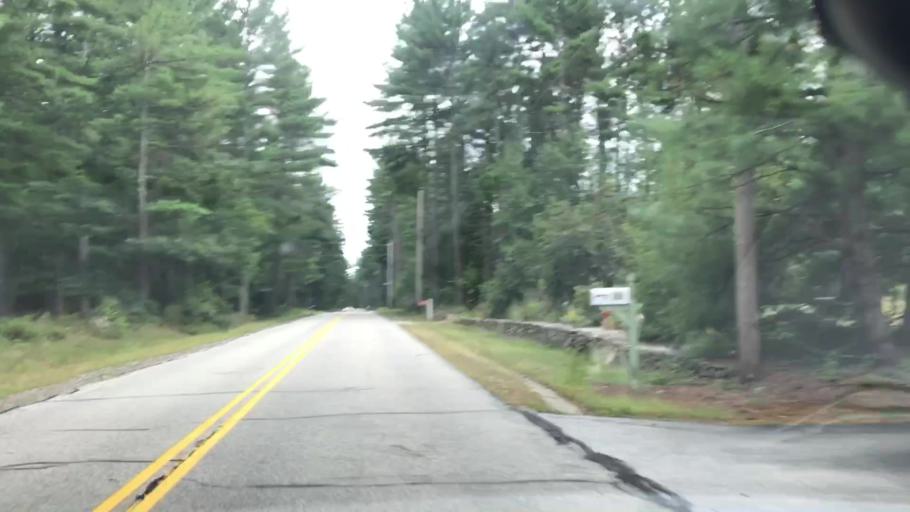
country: US
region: New Hampshire
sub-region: Hillsborough County
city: Merrimack
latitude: 42.8482
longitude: -71.5702
